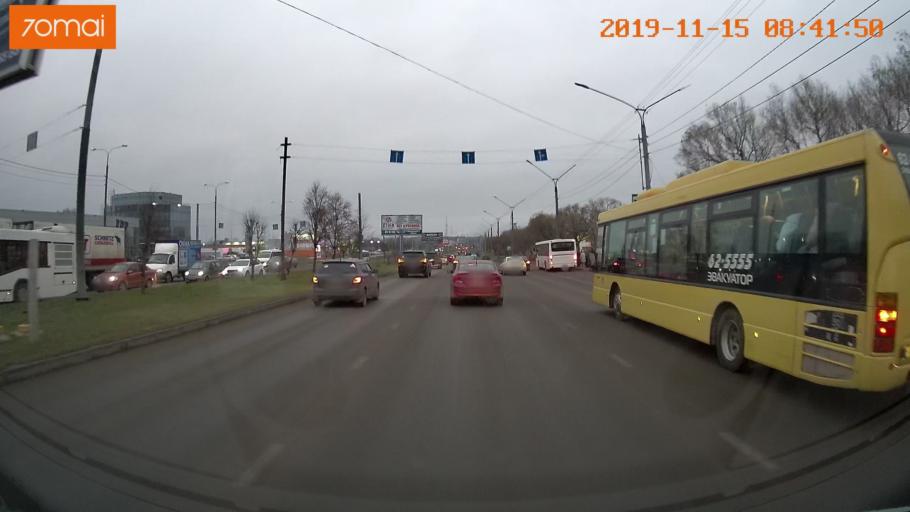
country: RU
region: Vologda
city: Cherepovets
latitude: 59.0986
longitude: 37.9112
